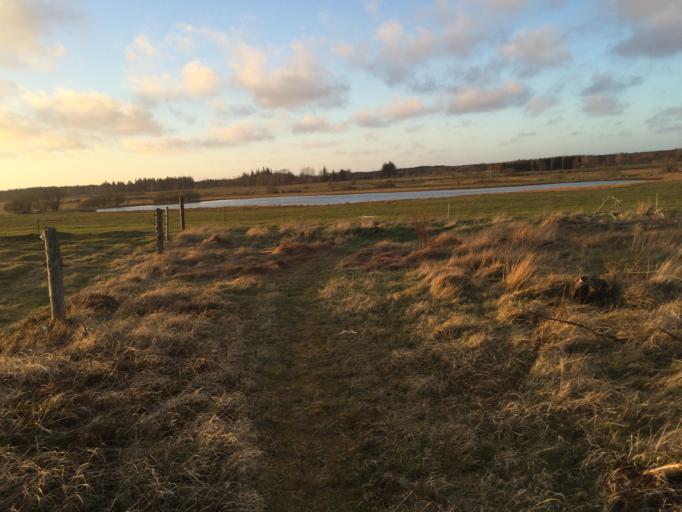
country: DK
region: Central Jutland
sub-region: Holstebro Kommune
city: Ulfborg
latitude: 56.2460
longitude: 8.4079
